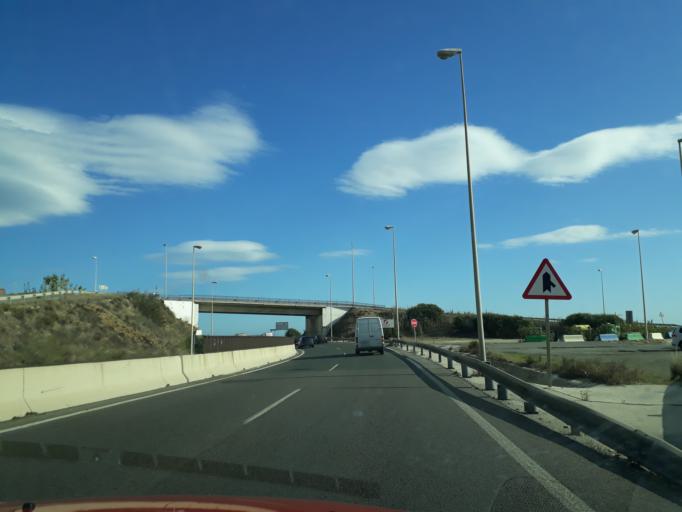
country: ES
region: Andalusia
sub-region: Provincia de Malaga
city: Fuengirola
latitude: 36.5074
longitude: -4.6449
